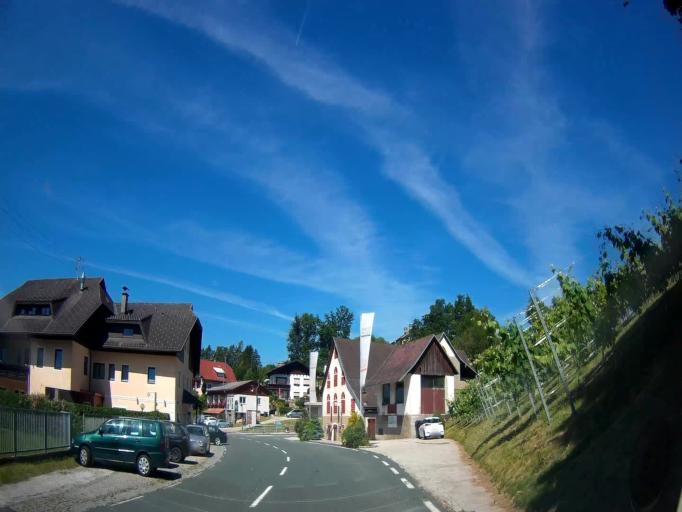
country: AT
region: Carinthia
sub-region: Politischer Bezirk Sankt Veit an der Glan
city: St. Georgen am Laengsee
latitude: 46.7627
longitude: 14.4251
